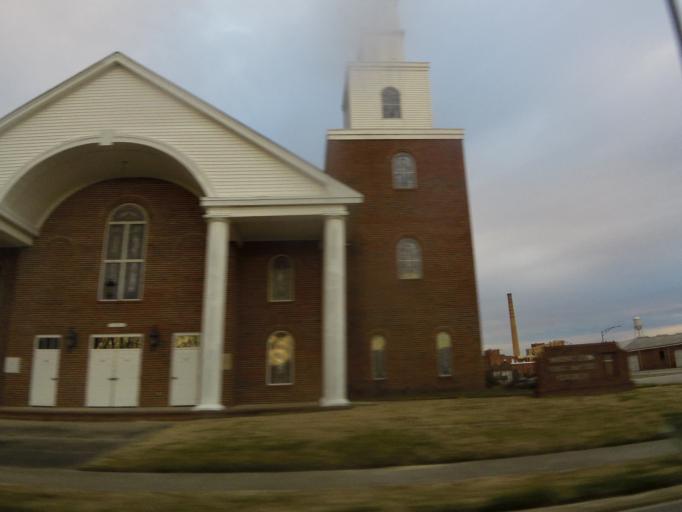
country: US
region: North Carolina
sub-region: Nash County
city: Rocky Mount
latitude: 35.9453
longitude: -77.7983
